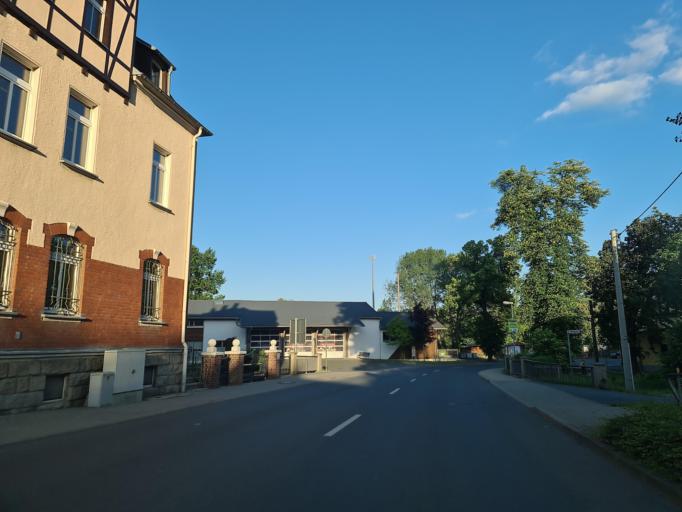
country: DE
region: Saxony
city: Weischlitz
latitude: 50.4474
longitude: 12.0592
